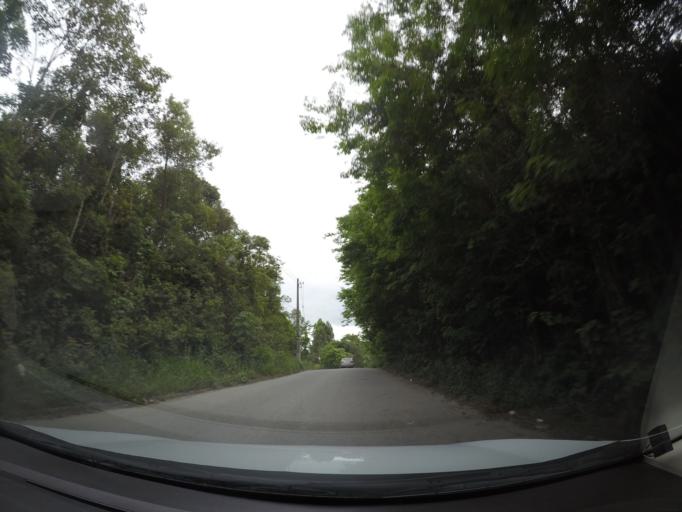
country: BR
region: Sao Paulo
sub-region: Aruja
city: Aruja
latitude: -23.3588
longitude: -46.2887
